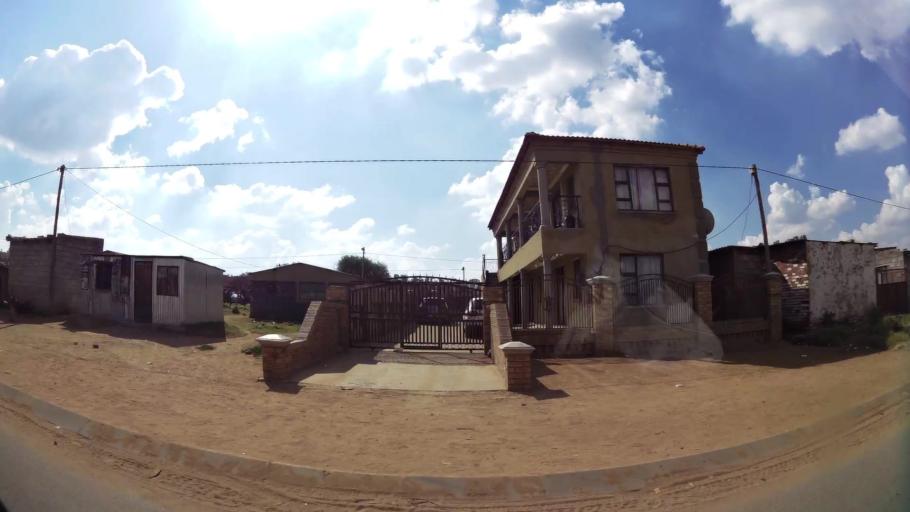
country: ZA
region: Gauteng
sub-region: City of Johannesburg Metropolitan Municipality
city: Roodepoort
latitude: -26.1902
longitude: 27.8719
